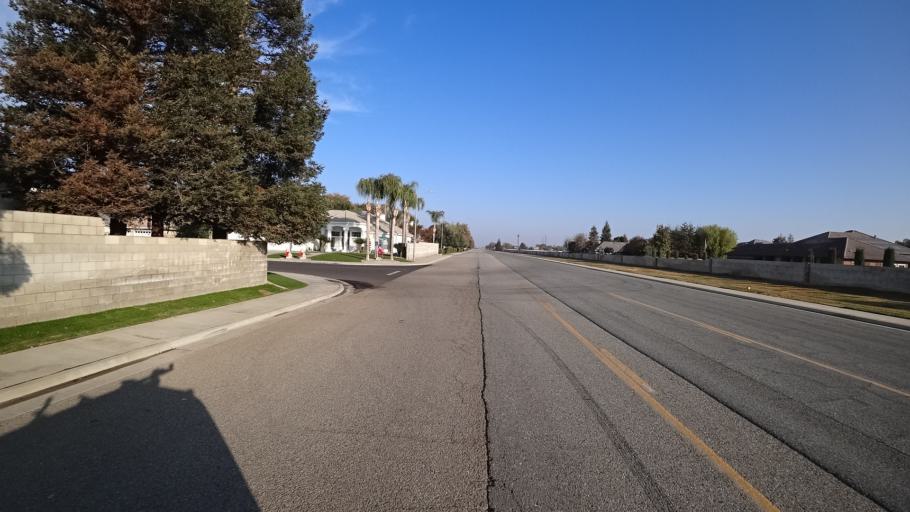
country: US
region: California
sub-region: Kern County
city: Rosedale
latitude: 35.3791
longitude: -119.1722
